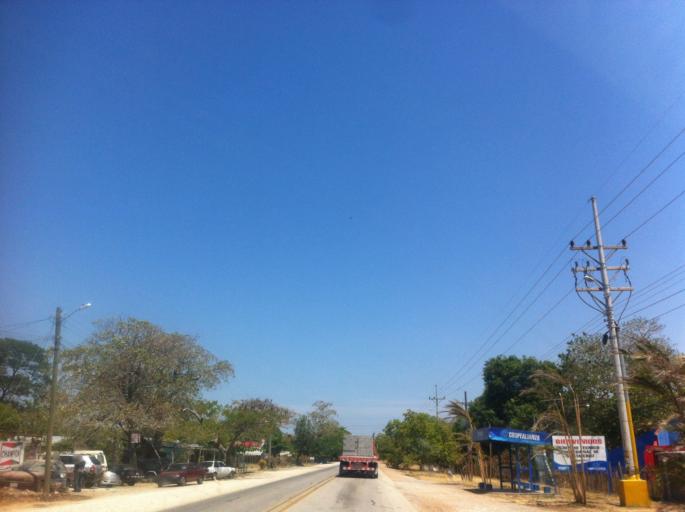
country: CR
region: Guanacaste
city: Santa Cruz
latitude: 10.2546
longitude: -85.5637
